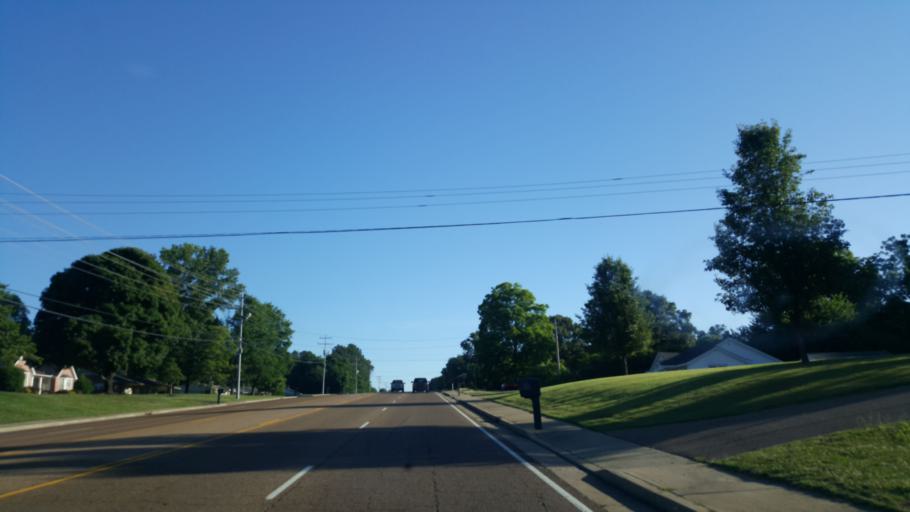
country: US
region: Tennessee
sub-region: Henderson County
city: Lexington
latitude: 35.6728
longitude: -88.3847
